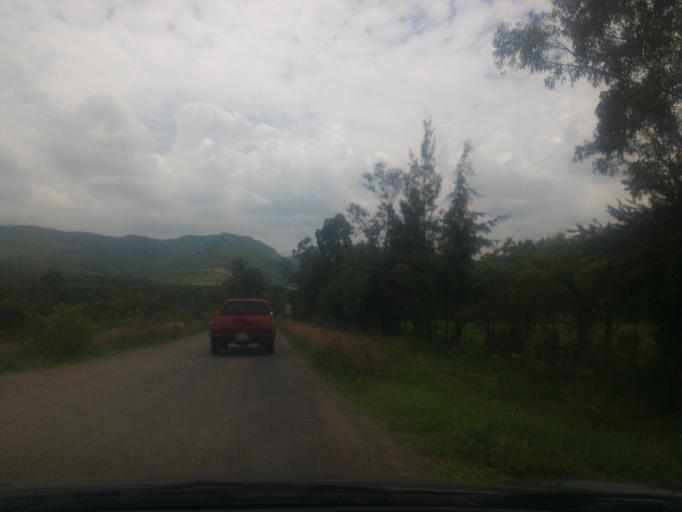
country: MX
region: Guanajuato
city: Ciudad Manuel Doblado
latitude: 20.8075
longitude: -102.0712
